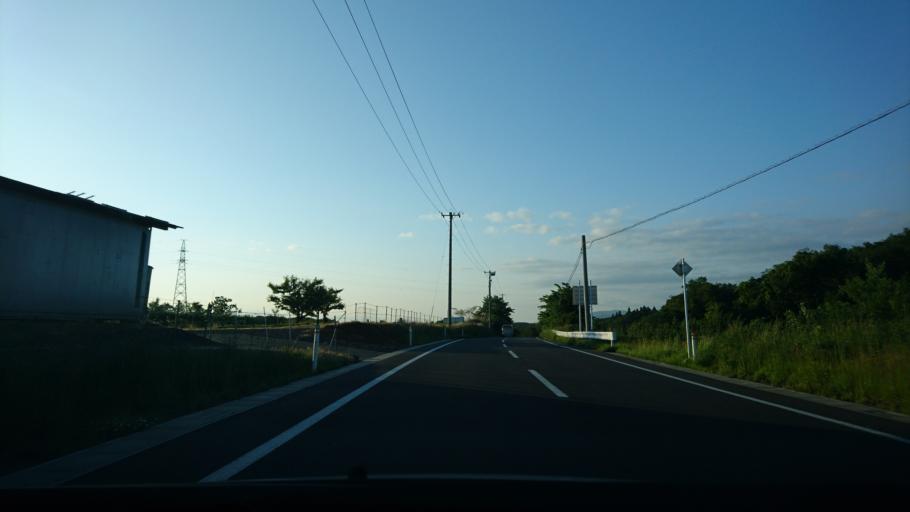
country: JP
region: Iwate
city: Ichinoseki
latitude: 38.8799
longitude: 141.1589
